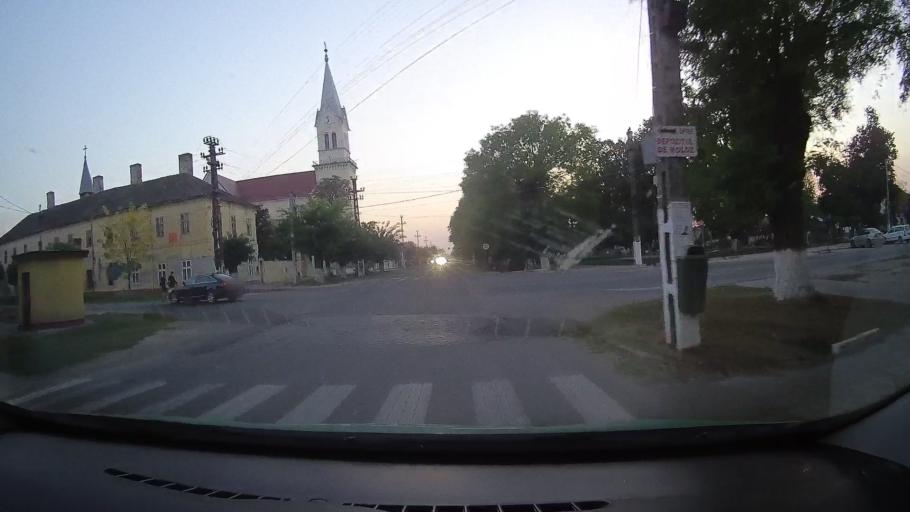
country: RO
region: Arad
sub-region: Comuna Santana
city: Santana
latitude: 46.3425
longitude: 21.4976
